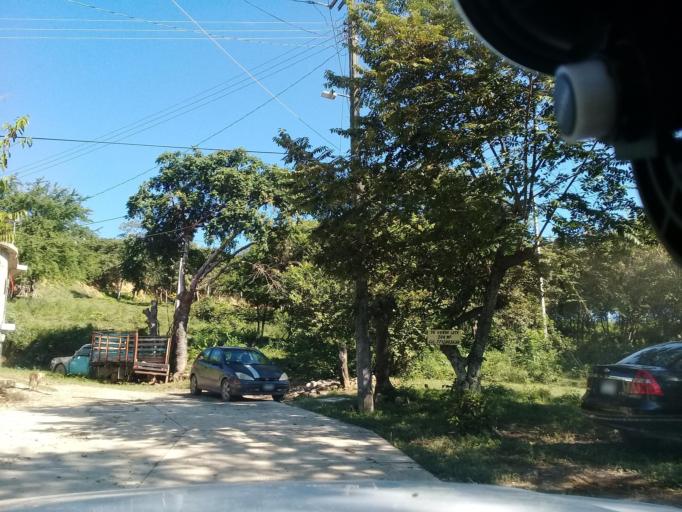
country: MX
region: Hidalgo
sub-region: Huejutla de Reyes
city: Huejutla de Reyes
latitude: 21.1609
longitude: -98.4106
